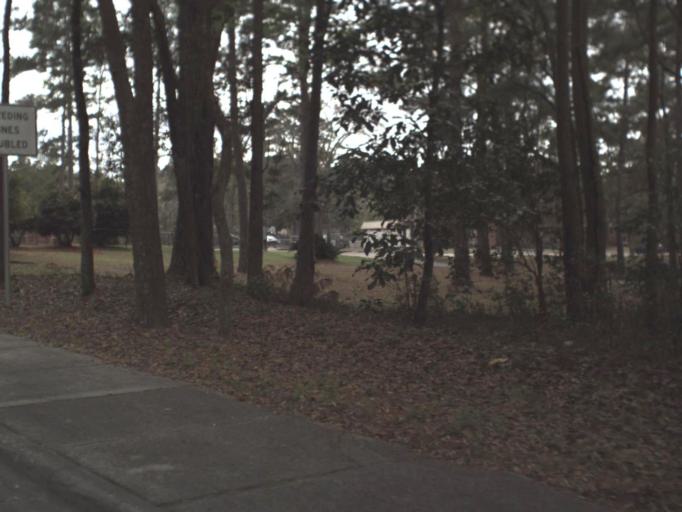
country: US
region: Florida
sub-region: Leon County
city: Tallahassee
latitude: 30.4881
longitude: -84.2774
